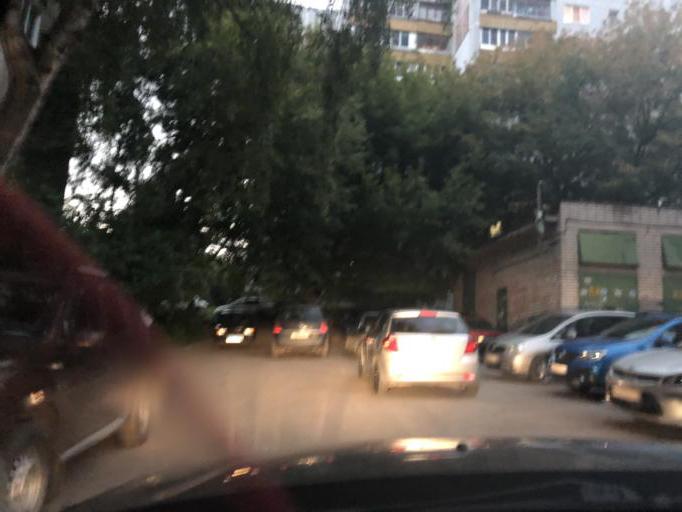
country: RU
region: Tula
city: Tula
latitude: 54.2165
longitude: 37.6091
